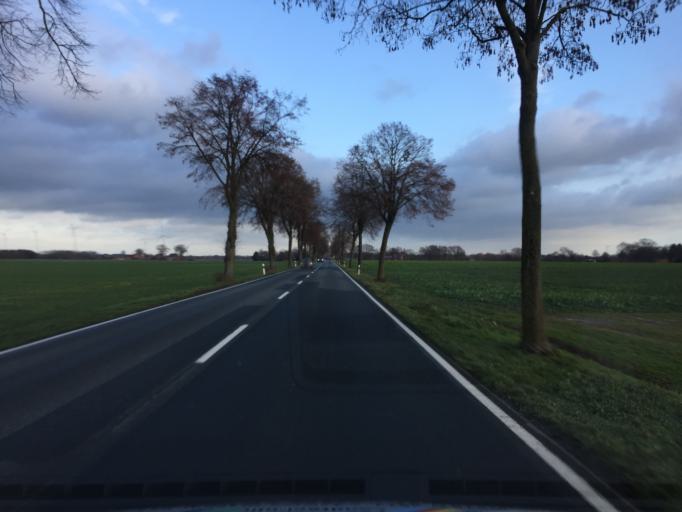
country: DE
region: Lower Saxony
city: Raddestorf
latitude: 52.4708
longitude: 8.9839
